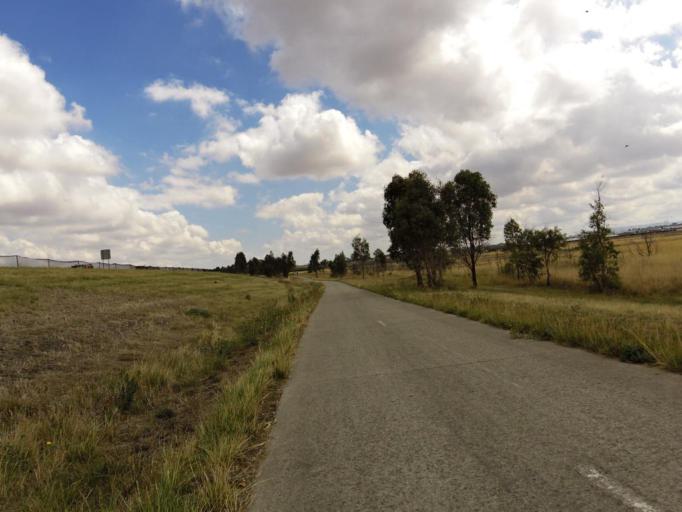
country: AU
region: Victoria
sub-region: Whittlesea
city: Epping
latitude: -37.6260
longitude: 144.9941
